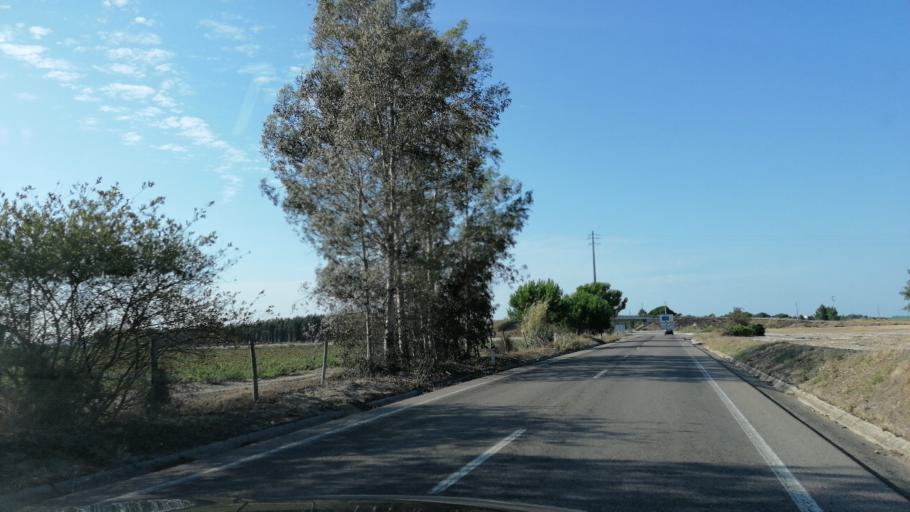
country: PT
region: Santarem
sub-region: Almeirim
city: Almeirim
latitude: 39.1696
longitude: -8.6205
